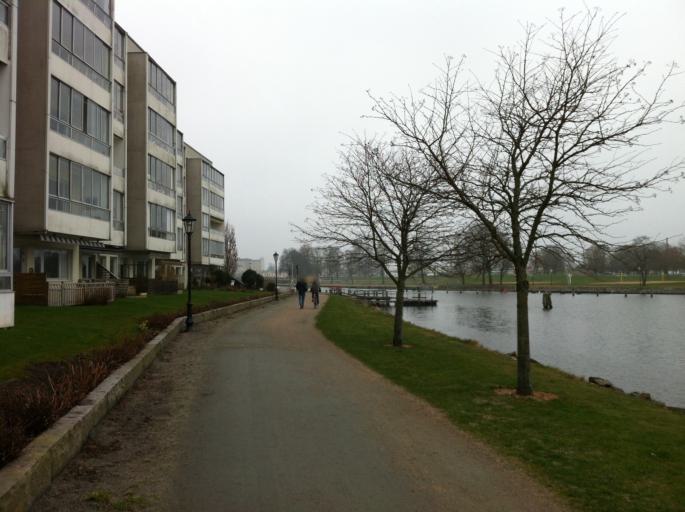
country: SE
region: Vaestra Goetaland
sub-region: Vanersborgs Kommun
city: Vanersborg
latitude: 58.3840
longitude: 12.3206
